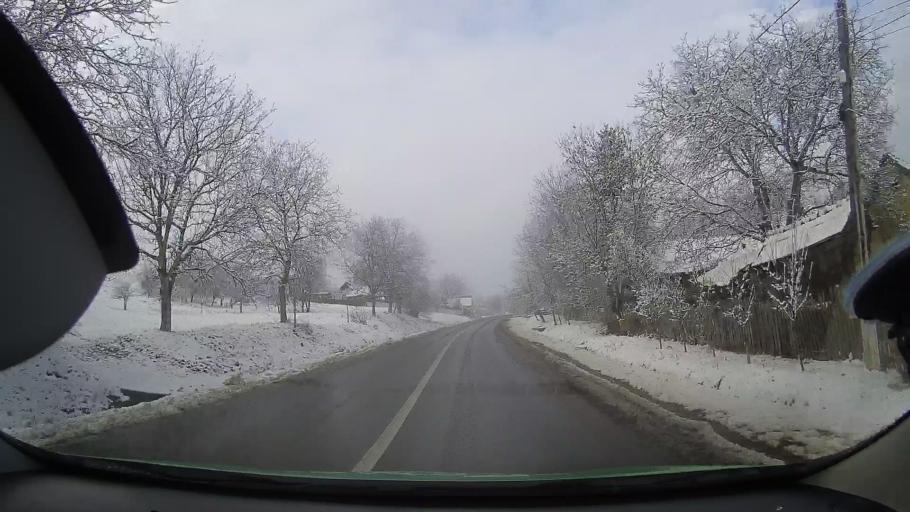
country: RO
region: Mures
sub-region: Comuna Atintis
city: Atintis
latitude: 46.4351
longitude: 24.0964
